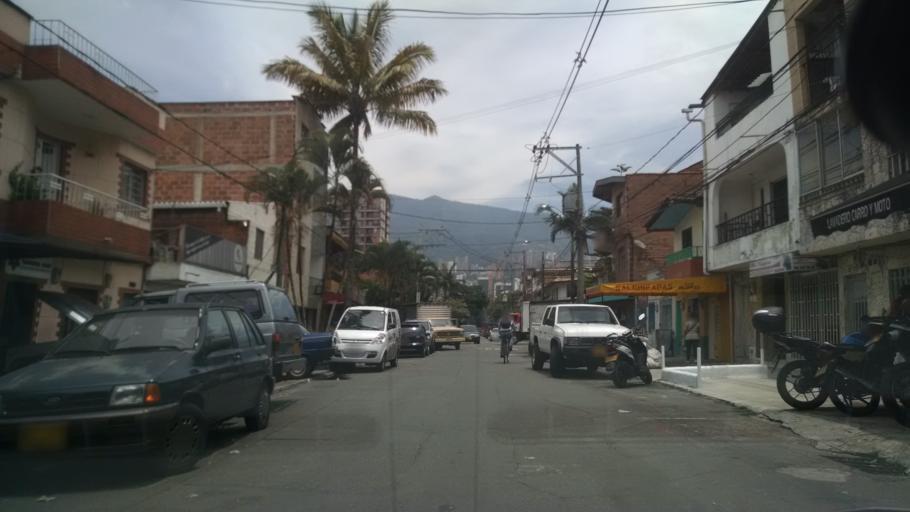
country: CO
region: Antioquia
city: Itagui
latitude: 6.2057
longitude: -75.5855
